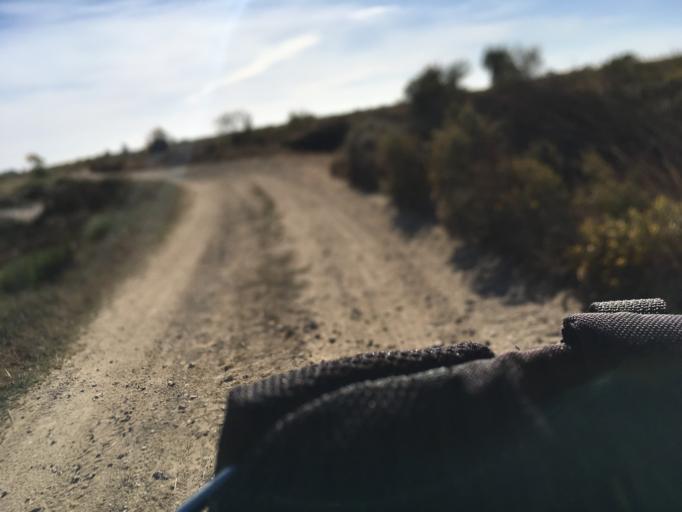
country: PT
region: Aveiro
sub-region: Estarreja
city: Salreu
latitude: 40.7269
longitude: -8.5730
